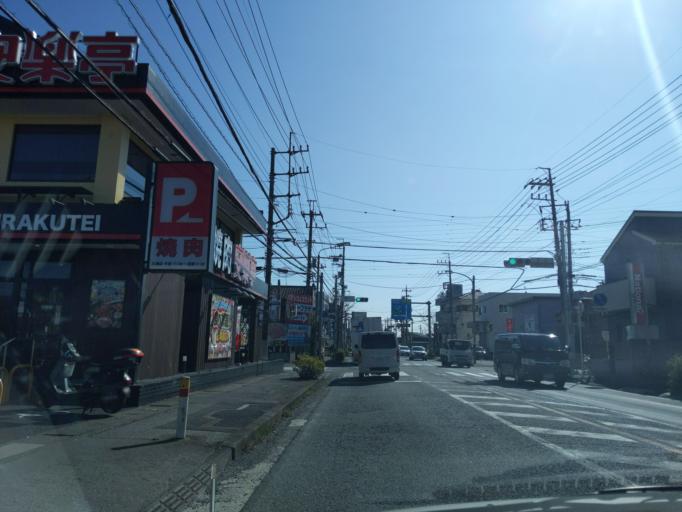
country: JP
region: Saitama
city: Yashio-shi
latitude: 35.8207
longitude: 139.8258
